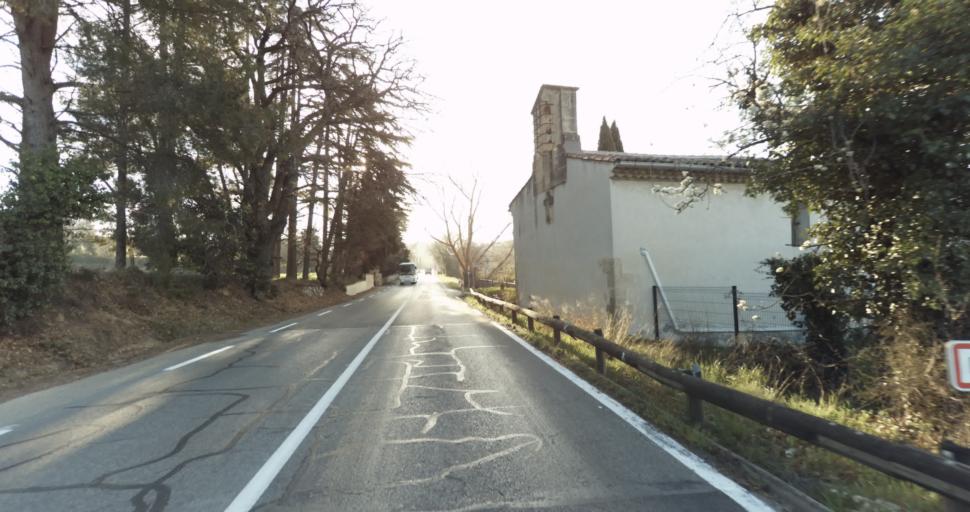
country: FR
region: Provence-Alpes-Cote d'Azur
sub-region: Departement des Bouches-du-Rhone
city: Eguilles
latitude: 43.5359
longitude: 5.3898
